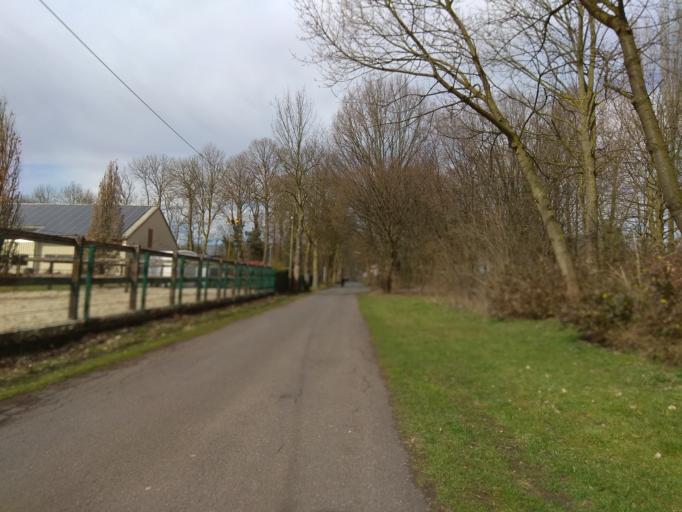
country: DE
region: North Rhine-Westphalia
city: Marl
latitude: 51.6414
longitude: 7.0864
